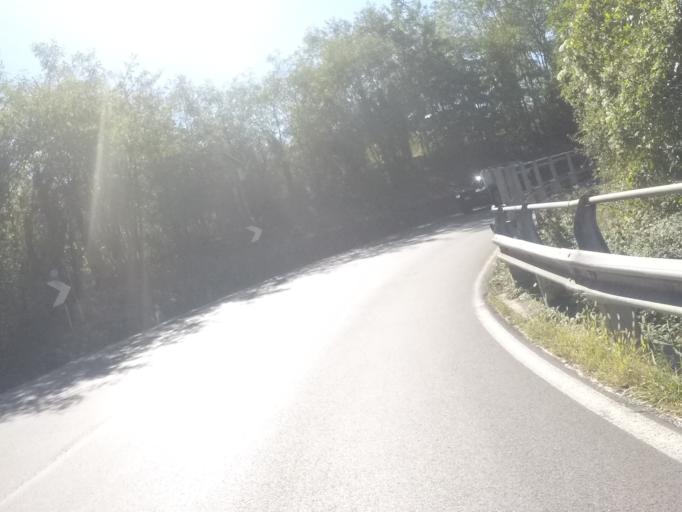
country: IT
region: Tuscany
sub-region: Province of Florence
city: Incisa in Val d'Arno
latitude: 43.6779
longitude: 11.4637
